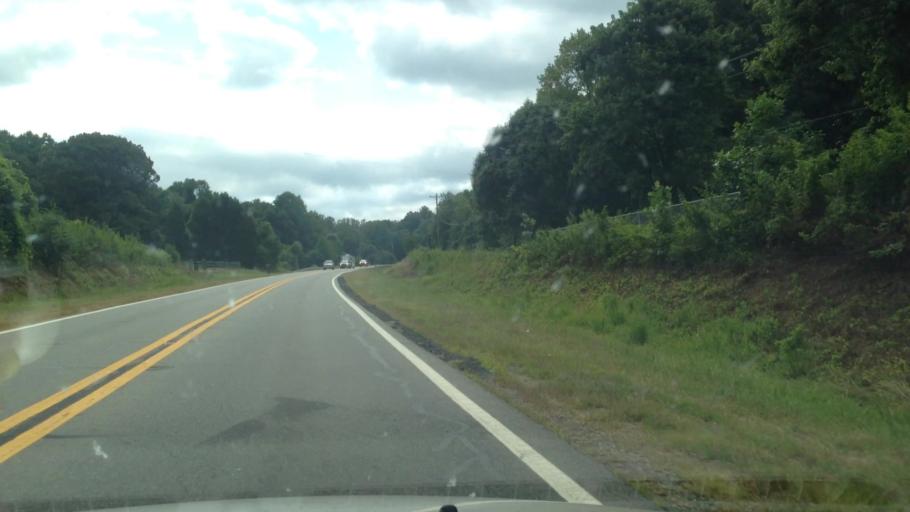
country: US
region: North Carolina
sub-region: Rockingham County
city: Madison
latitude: 36.3801
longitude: -79.8666
